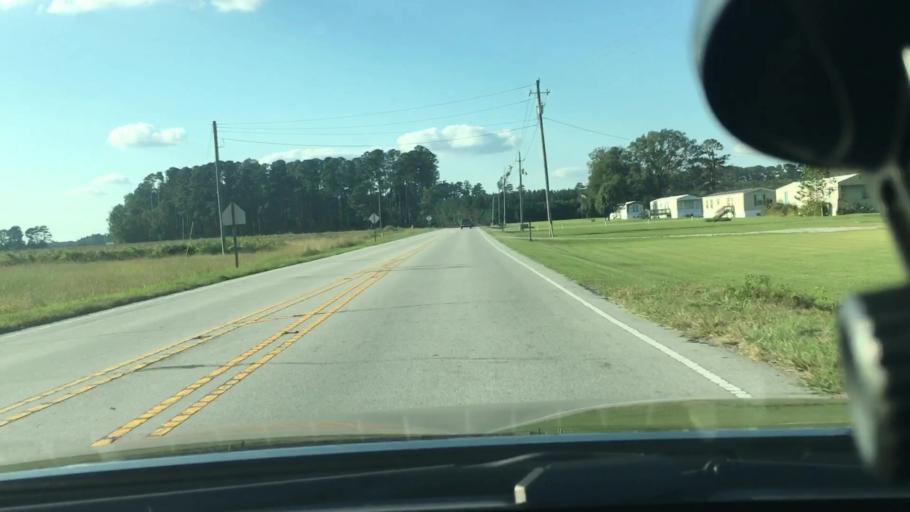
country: US
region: North Carolina
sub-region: Pitt County
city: Windsor
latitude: 35.4656
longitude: -77.2761
